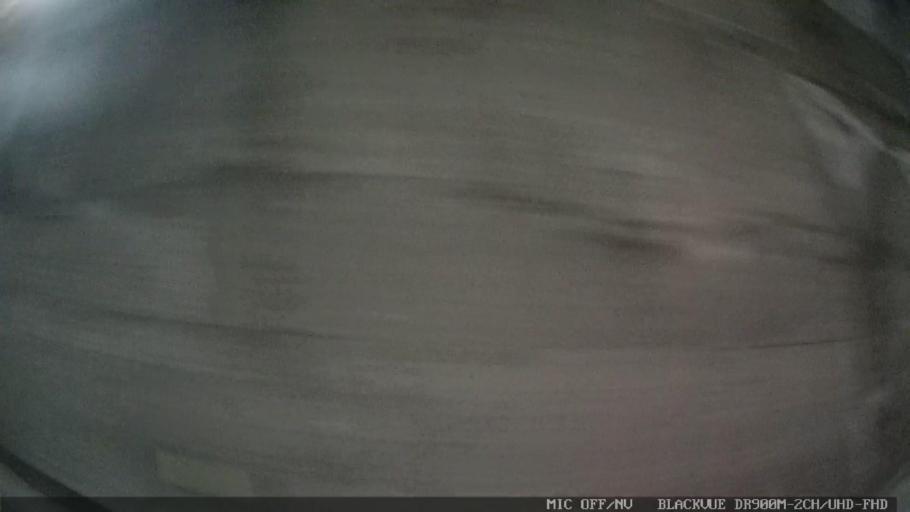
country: BR
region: Sao Paulo
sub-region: Cubatao
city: Cubatao
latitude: -23.8910
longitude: -46.5059
